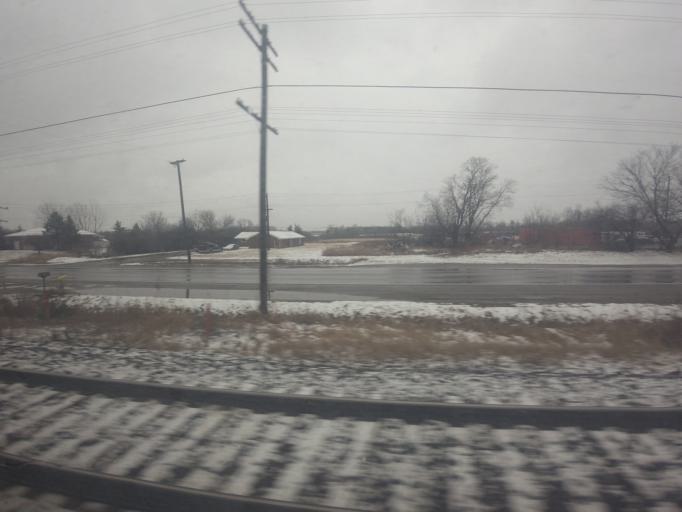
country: CA
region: Ontario
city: Belleville
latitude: 44.1624
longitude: -77.4339
